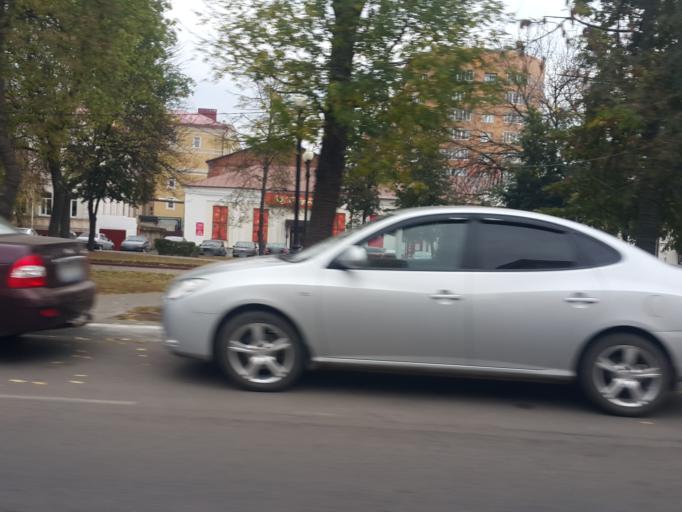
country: RU
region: Tambov
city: Tambov
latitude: 52.7238
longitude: 41.4513
